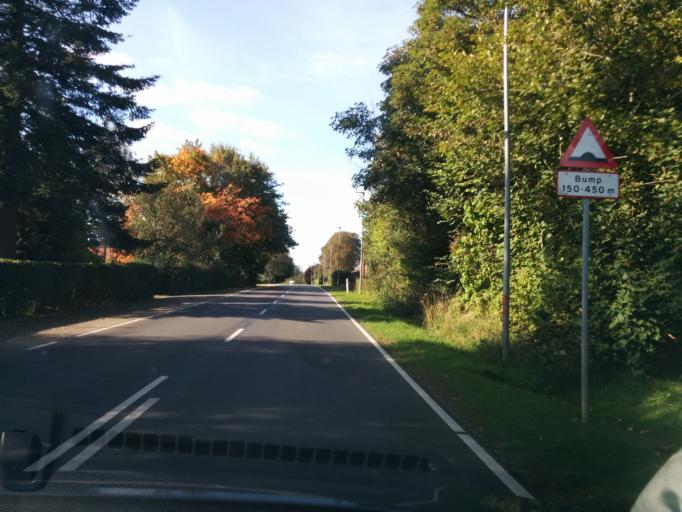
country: DK
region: South Denmark
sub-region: Kolding Kommune
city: Sonder Bjert
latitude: 55.4050
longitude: 9.5376
